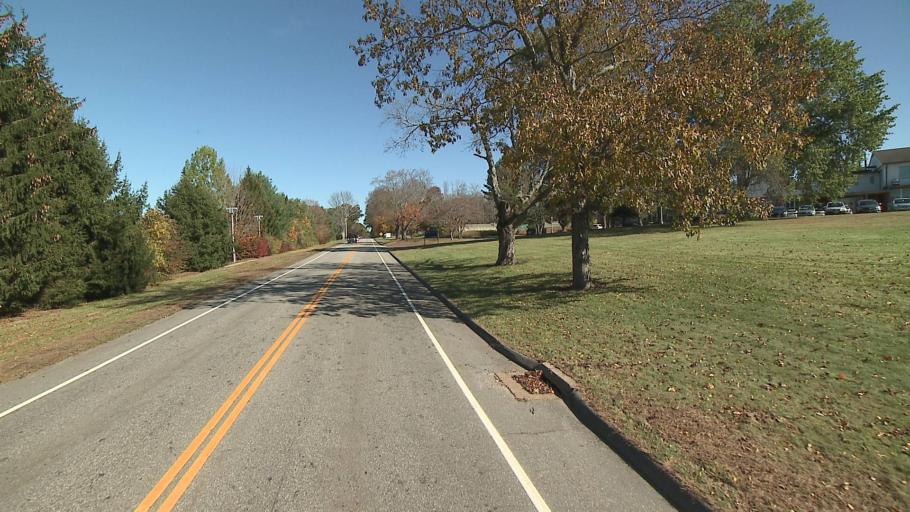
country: US
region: Connecticut
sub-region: Tolland County
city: South Coventry
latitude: 41.8119
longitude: -72.2967
